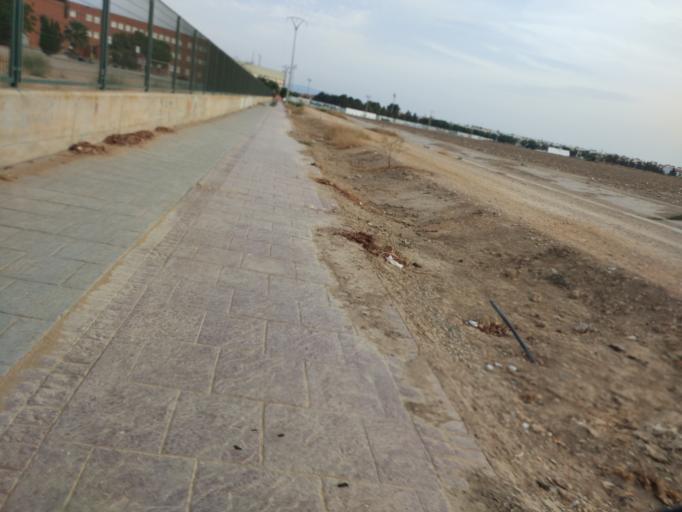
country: ES
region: Murcia
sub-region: Murcia
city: Los Alcazares
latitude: 37.7441
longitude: -0.8583
